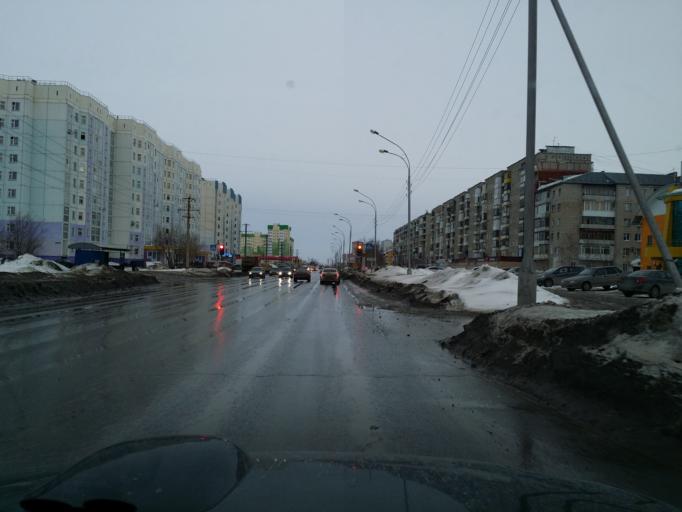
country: RU
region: Khanty-Mansiyskiy Avtonomnyy Okrug
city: Nizhnevartovsk
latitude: 60.9383
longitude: 76.6166
